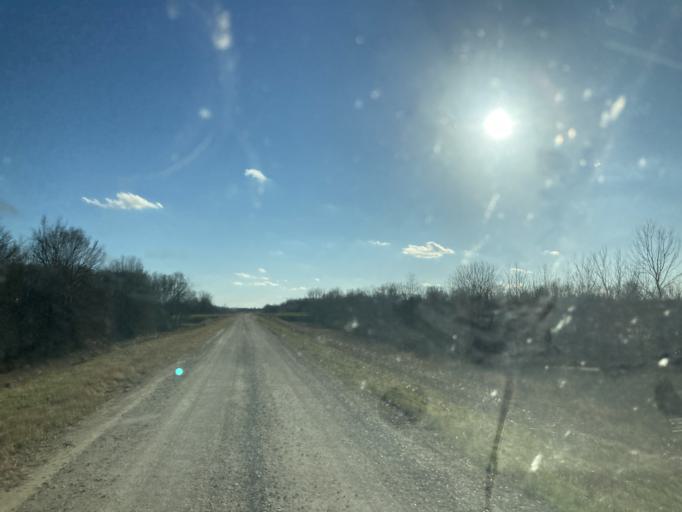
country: US
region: Mississippi
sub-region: Yazoo County
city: Yazoo City
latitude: 32.9192
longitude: -90.5536
